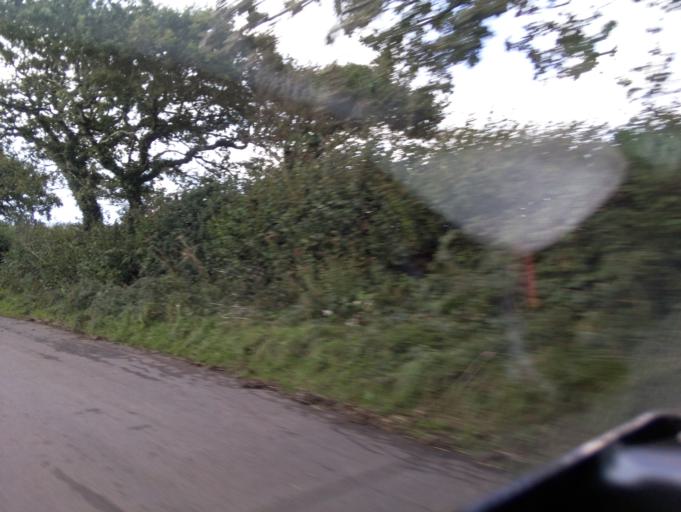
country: GB
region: England
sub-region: Devon
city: South Brent
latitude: 50.3785
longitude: -3.7613
